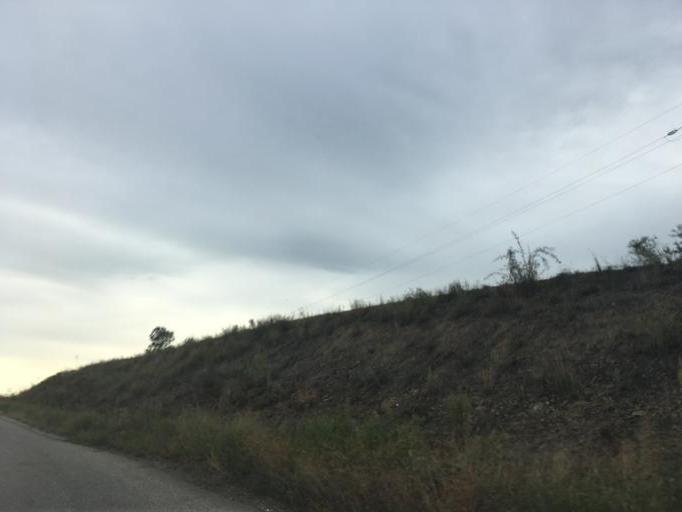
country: FR
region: Rhone-Alpes
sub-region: Departement de la Loire
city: Saint-Martin-la-Plaine
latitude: 45.5401
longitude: 4.5994
